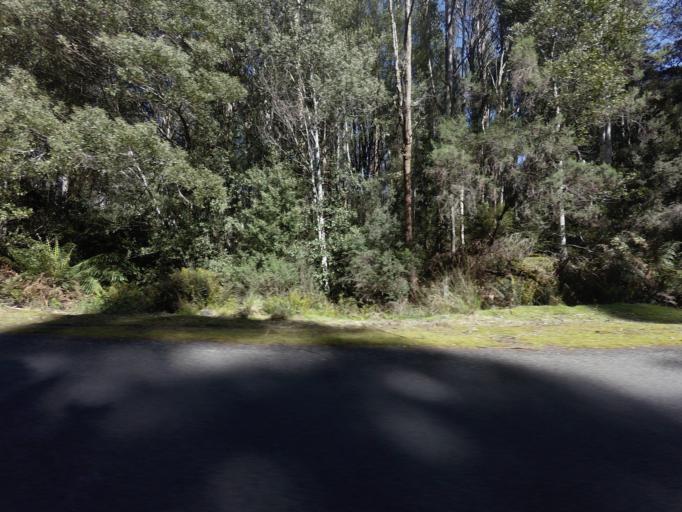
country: AU
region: Tasmania
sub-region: Derwent Valley
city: New Norfolk
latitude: -42.7668
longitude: 146.5904
